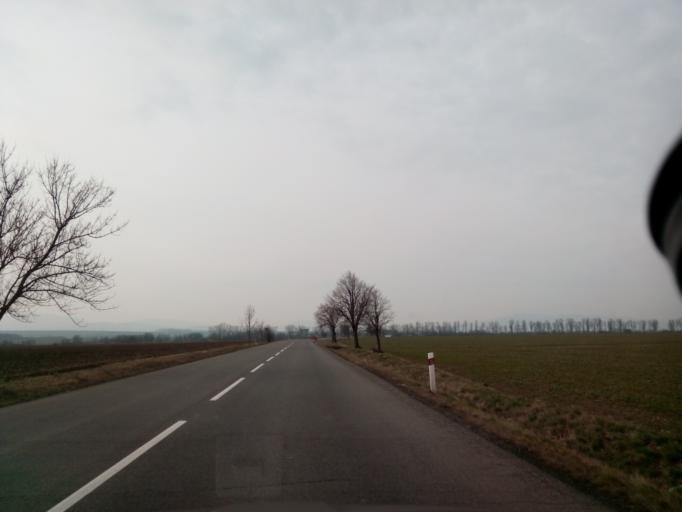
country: SK
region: Kosicky
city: Trebisov
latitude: 48.5489
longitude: 21.6890
